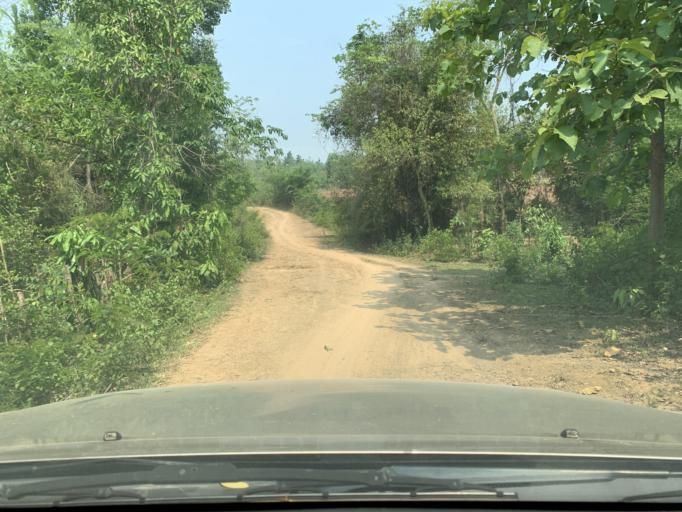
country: LA
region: Louangphabang
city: Louangphabang
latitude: 19.9384
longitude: 102.1458
